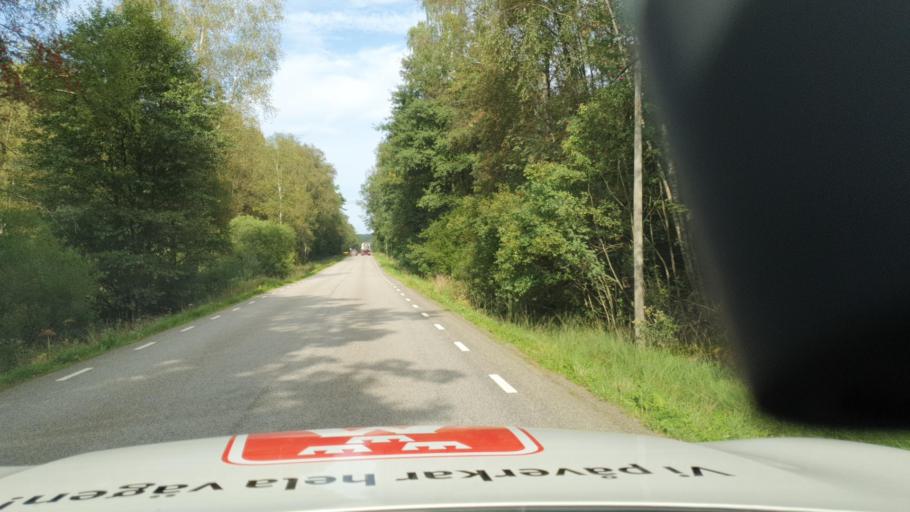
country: SE
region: Vaestra Goetaland
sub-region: Marks Kommun
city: Kinna
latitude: 57.4026
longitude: 12.6736
